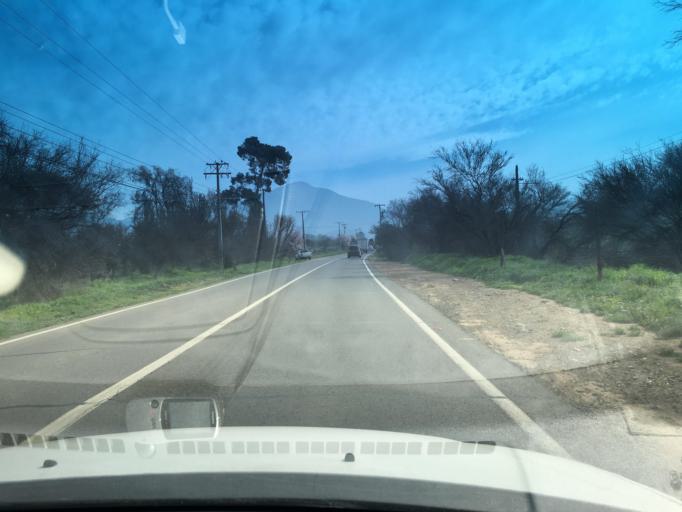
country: CL
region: Santiago Metropolitan
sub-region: Provincia de Chacabuco
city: Lampa
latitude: -33.1232
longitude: -70.9244
